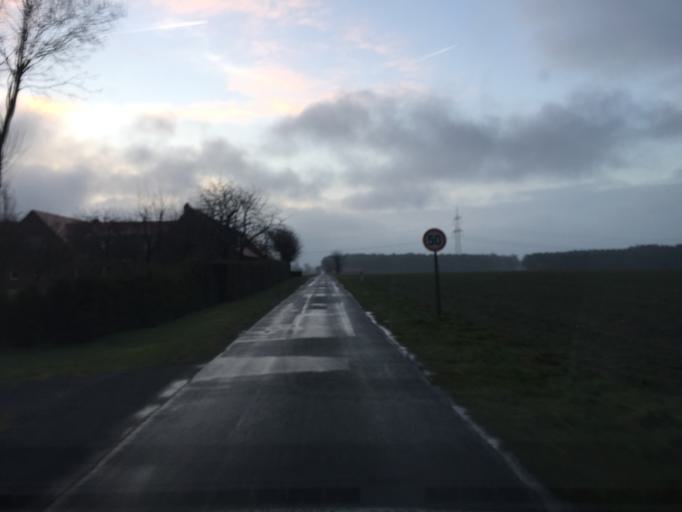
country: DE
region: Lower Saxony
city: Pennigsehl
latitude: 52.6593
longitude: 9.0229
